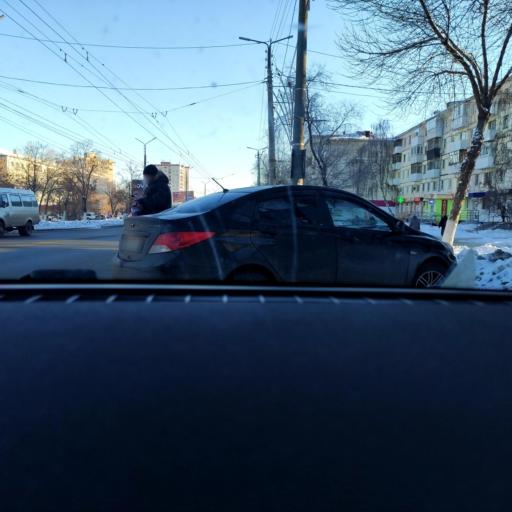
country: RU
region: Samara
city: Novokuybyshevsk
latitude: 53.0976
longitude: 49.9670
